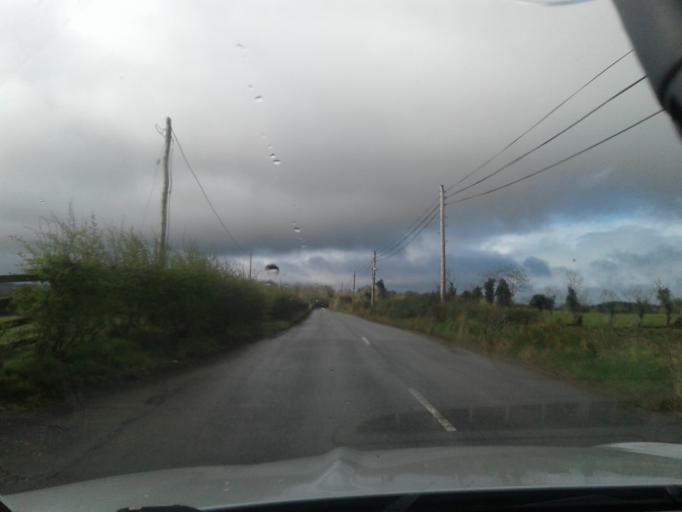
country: IE
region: Ulster
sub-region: County Donegal
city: Ramelton
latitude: 55.0522
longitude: -7.6390
